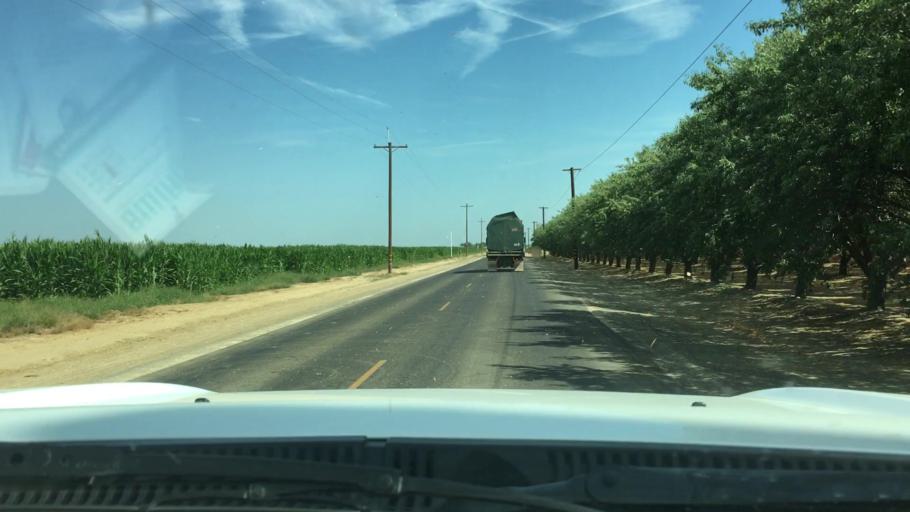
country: US
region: California
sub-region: Kern County
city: Shafter
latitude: 35.4801
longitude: -119.3680
